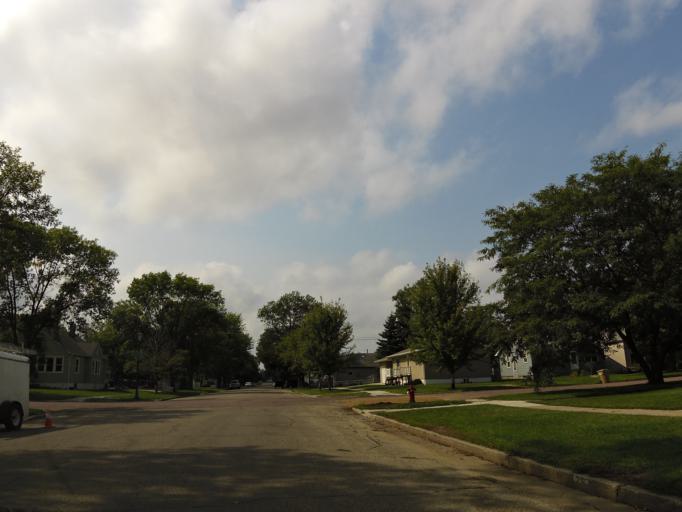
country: US
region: South Dakota
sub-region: Codington County
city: Watertown
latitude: 44.8973
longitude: -97.1171
